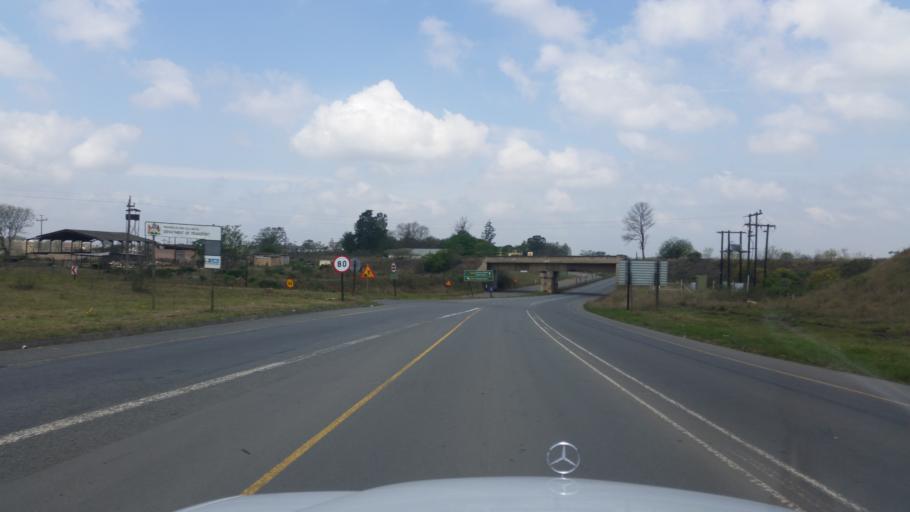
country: ZA
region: KwaZulu-Natal
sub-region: uMgungundlovu District Municipality
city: Camperdown
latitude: -29.7214
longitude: 30.4979
